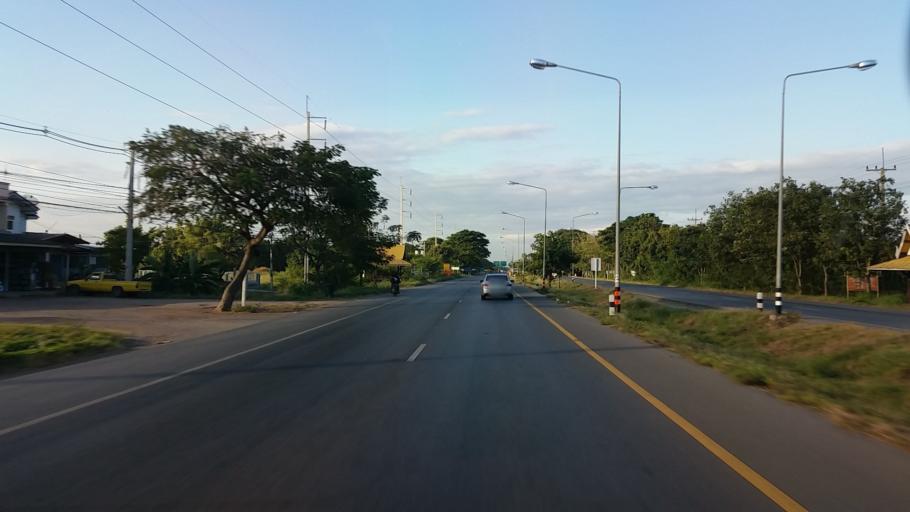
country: TH
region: Lop Buri
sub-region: Amphoe Tha Luang
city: Tha Luang
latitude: 15.0825
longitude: 101.0029
